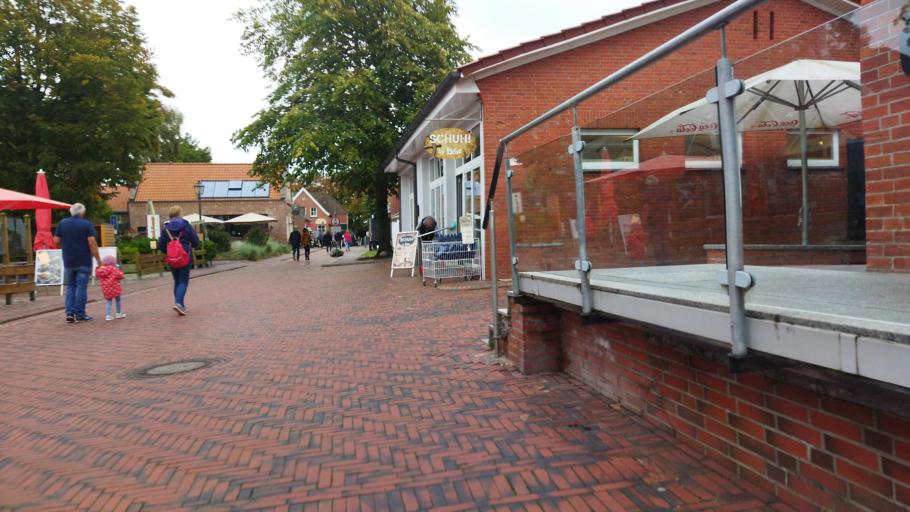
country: DE
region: Lower Saxony
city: Wirdum
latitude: 53.5016
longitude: 7.0933
